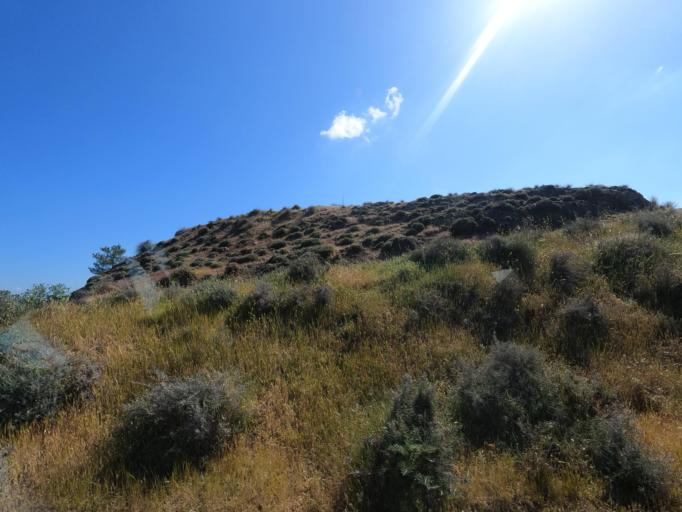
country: CY
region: Lefkosia
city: Peristerona
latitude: 35.0586
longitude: 33.0535
